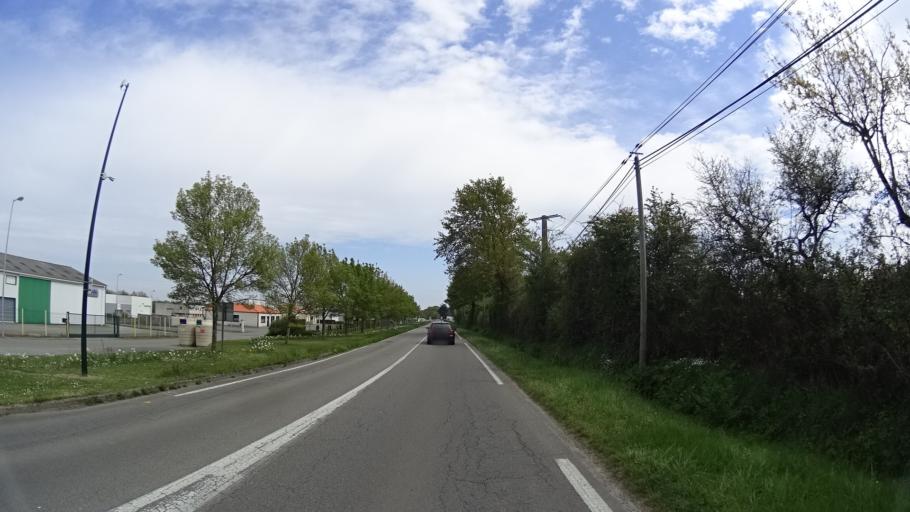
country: FR
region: Pays de la Loire
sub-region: Departement de la Loire-Atlantique
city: Sainte-Pazanne
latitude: 47.1032
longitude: -1.7996
